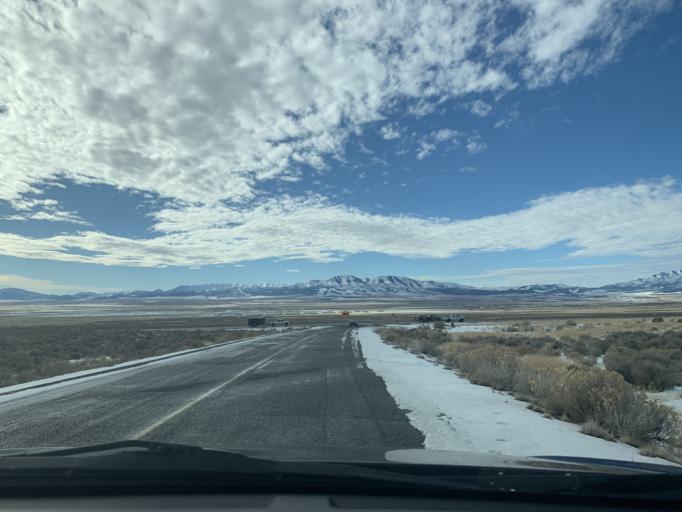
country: US
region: Utah
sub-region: Tooele County
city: Tooele
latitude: 40.2987
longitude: -112.2727
